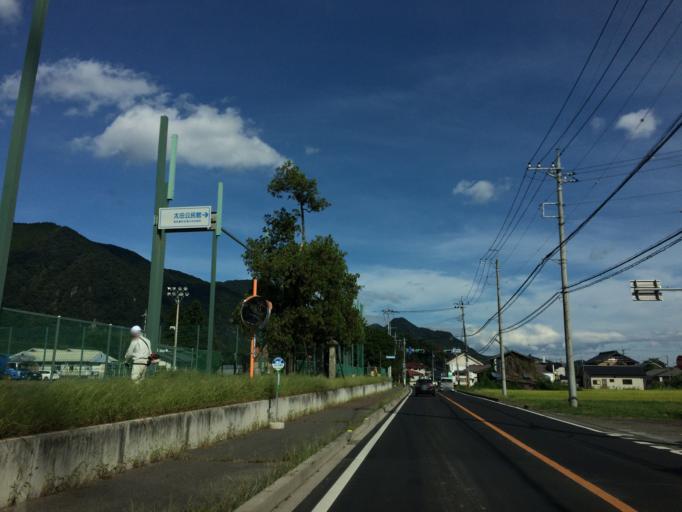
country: JP
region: Gunma
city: Nakanojomachi
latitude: 36.5725
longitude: 138.8644
